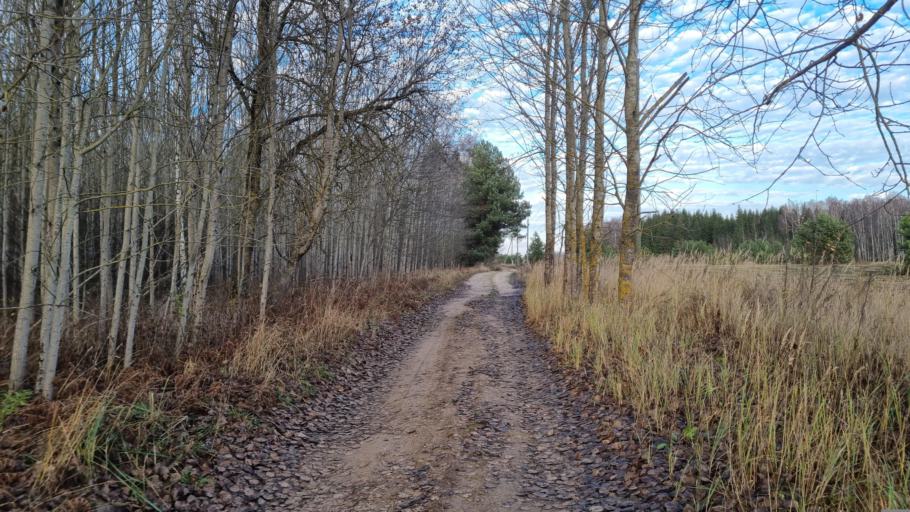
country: LV
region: Kekava
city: Kekava
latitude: 56.7829
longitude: 24.2468
